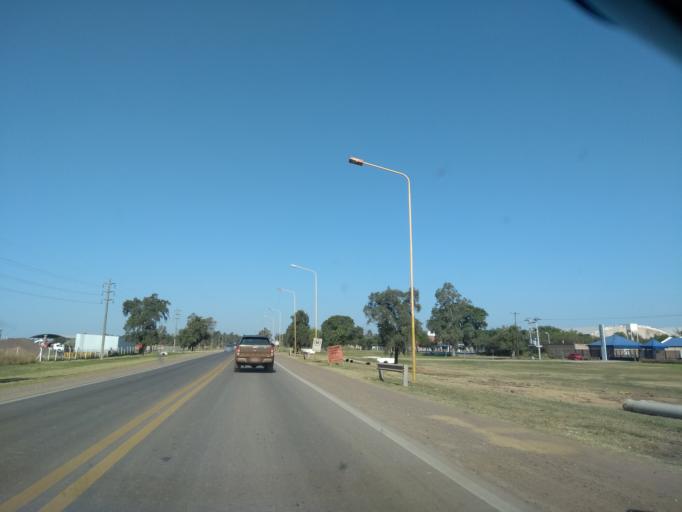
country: AR
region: Chaco
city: Presidencia Roque Saenz Pena
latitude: -26.8008
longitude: -60.4132
